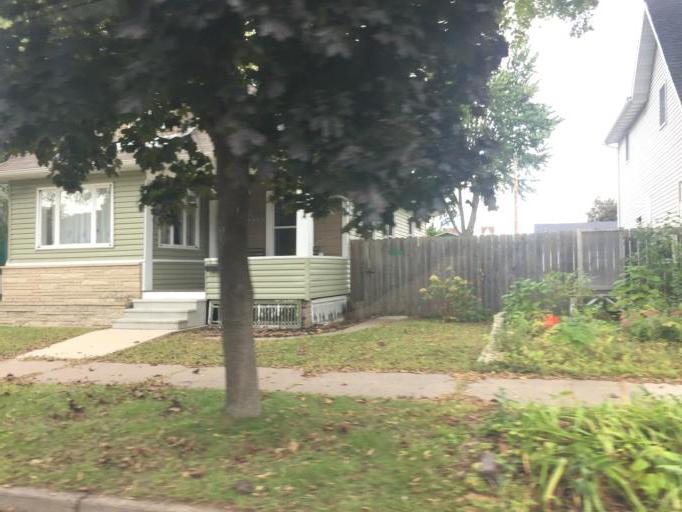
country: US
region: Minnesota
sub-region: Winona County
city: Winona
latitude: 44.0504
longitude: -91.6577
